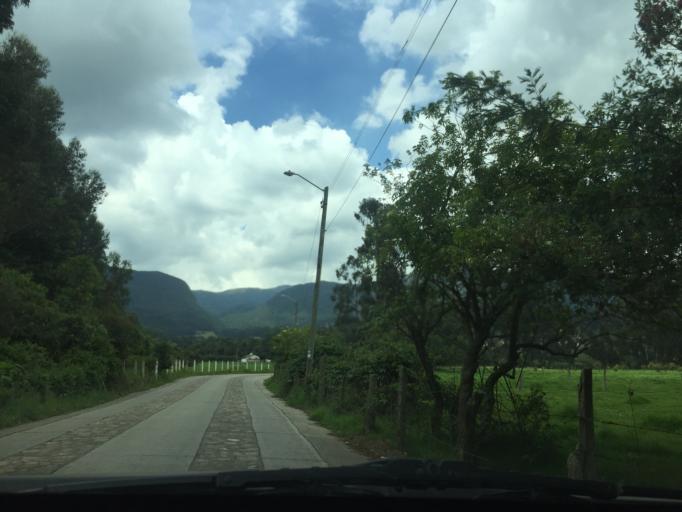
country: CO
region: Cundinamarca
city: Cogua
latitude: 5.0518
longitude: -73.9924
